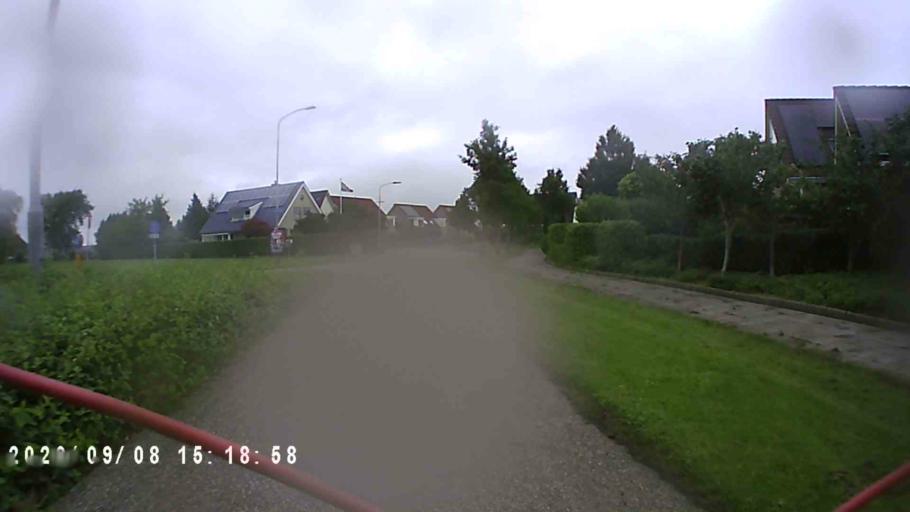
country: NL
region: Groningen
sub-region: Gemeente Bedum
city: Bedum
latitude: 53.2797
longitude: 6.6914
